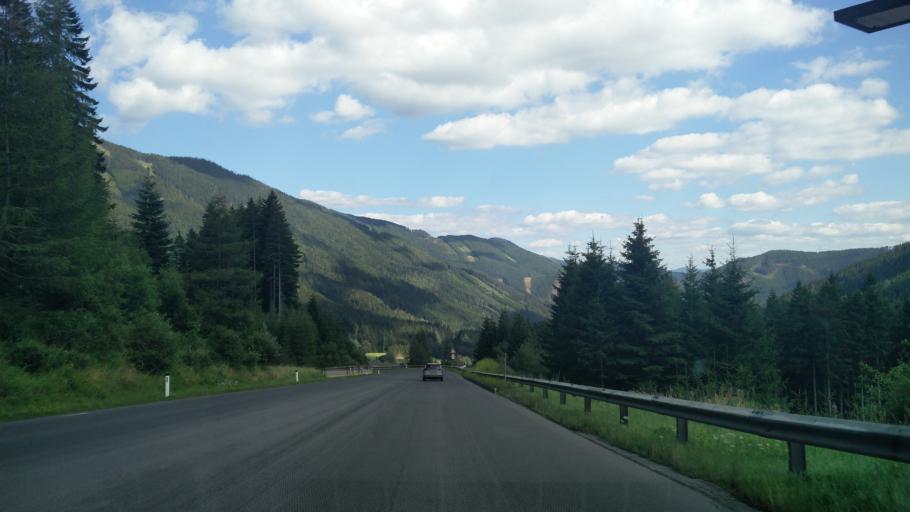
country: AT
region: Styria
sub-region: Politischer Bezirk Leoben
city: Vordernberg
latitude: 47.5183
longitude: 14.9615
